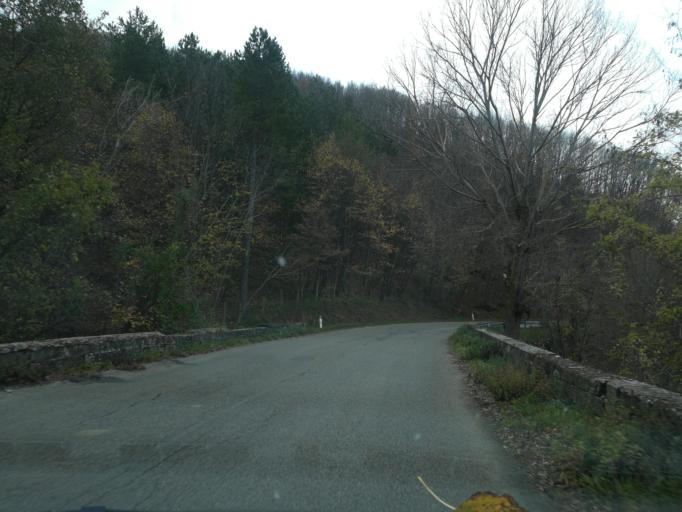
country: IT
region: Molise
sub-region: Provincia di Isernia
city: Agnone
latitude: 41.8221
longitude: 14.3772
